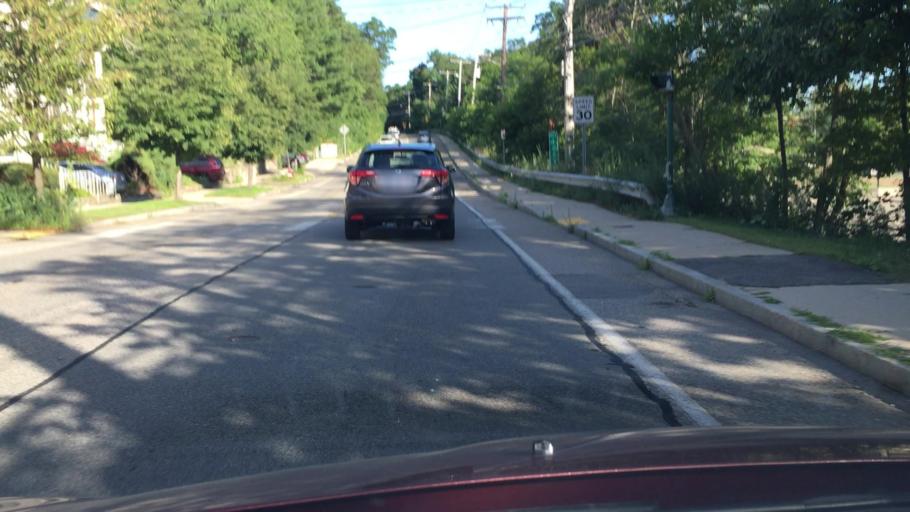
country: US
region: Massachusetts
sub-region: Middlesex County
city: Arlington
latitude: 42.4261
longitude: -71.1725
